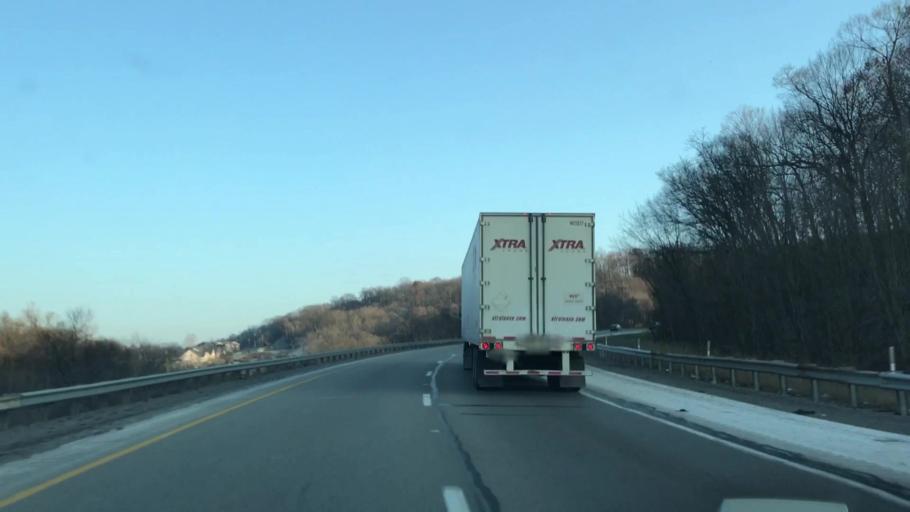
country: US
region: Pennsylvania
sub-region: Allegheny County
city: Emsworth
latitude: 40.5008
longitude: -80.1250
